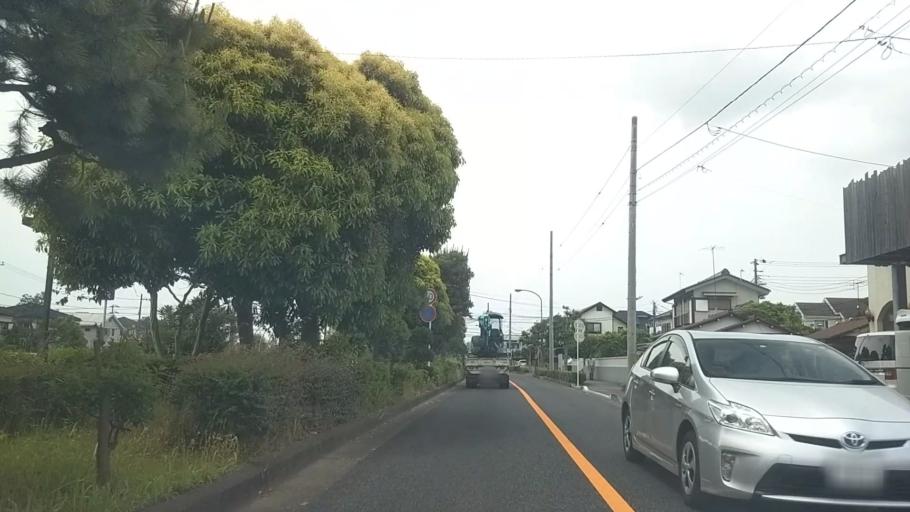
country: JP
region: Kanagawa
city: Fujisawa
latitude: 35.3303
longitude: 139.4653
